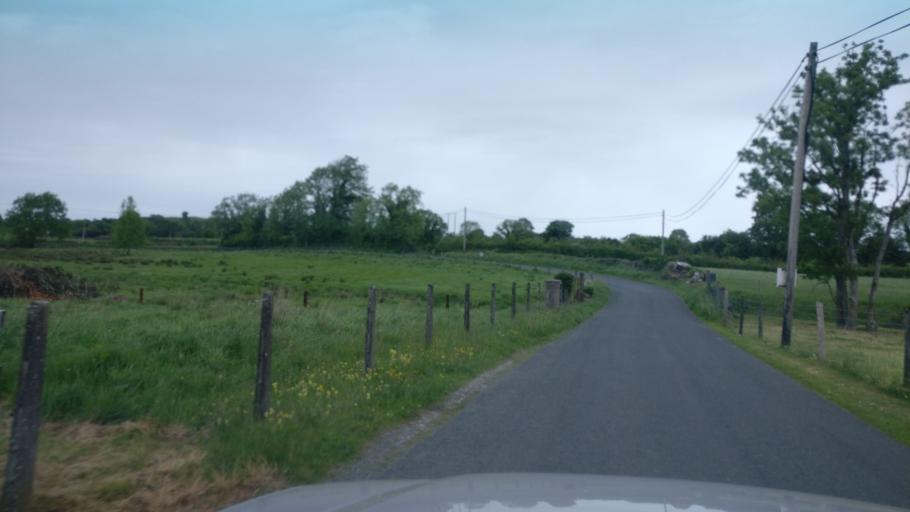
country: IE
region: Connaught
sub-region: County Galway
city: Loughrea
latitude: 53.1174
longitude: -8.4252
